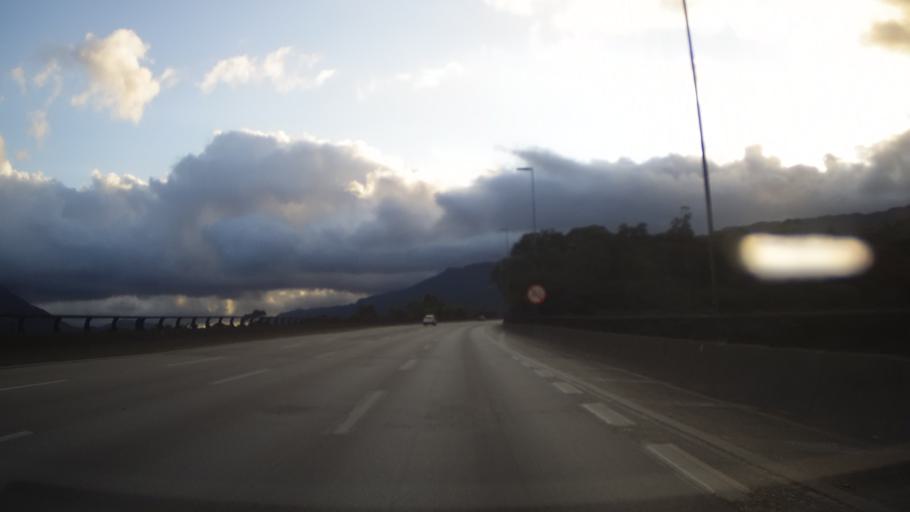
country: BR
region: Sao Paulo
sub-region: Cubatao
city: Cubatao
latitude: -23.8994
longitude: -46.4767
